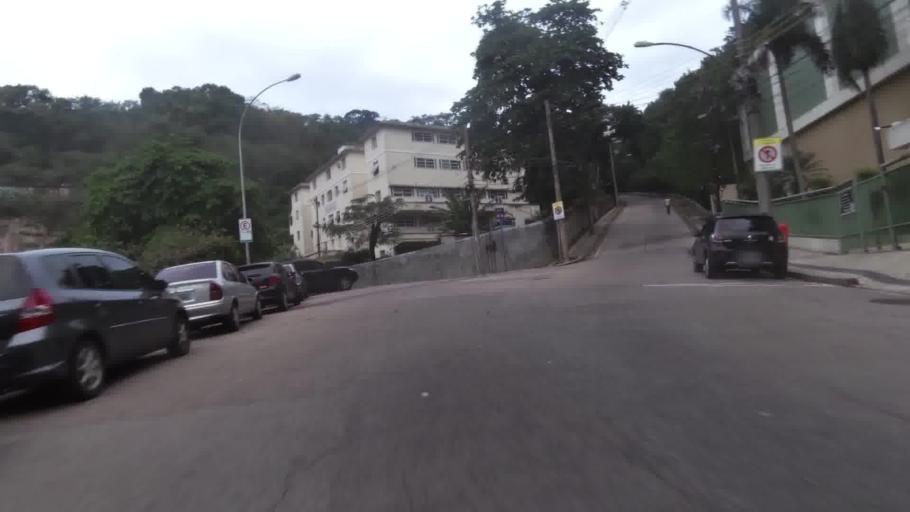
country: BR
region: Rio de Janeiro
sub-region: Rio De Janeiro
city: Rio de Janeiro
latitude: -22.9580
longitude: -43.1778
